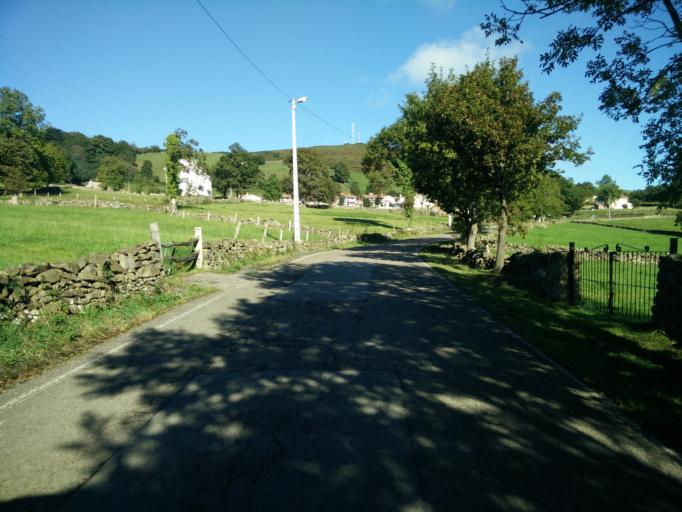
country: ES
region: Cantabria
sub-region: Provincia de Cantabria
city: San Pedro del Romeral
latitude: 43.1149
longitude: -3.8143
